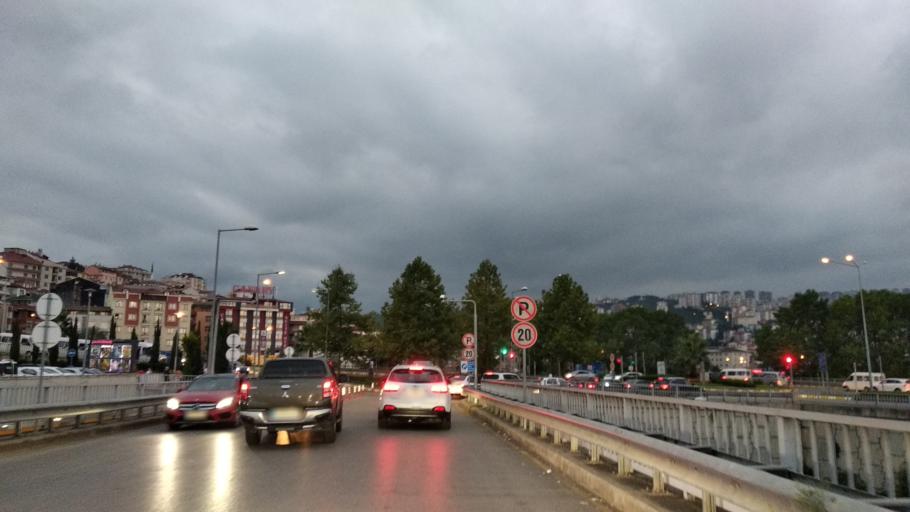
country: TR
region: Trabzon
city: Trabzon
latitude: 40.9998
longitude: 39.7590
